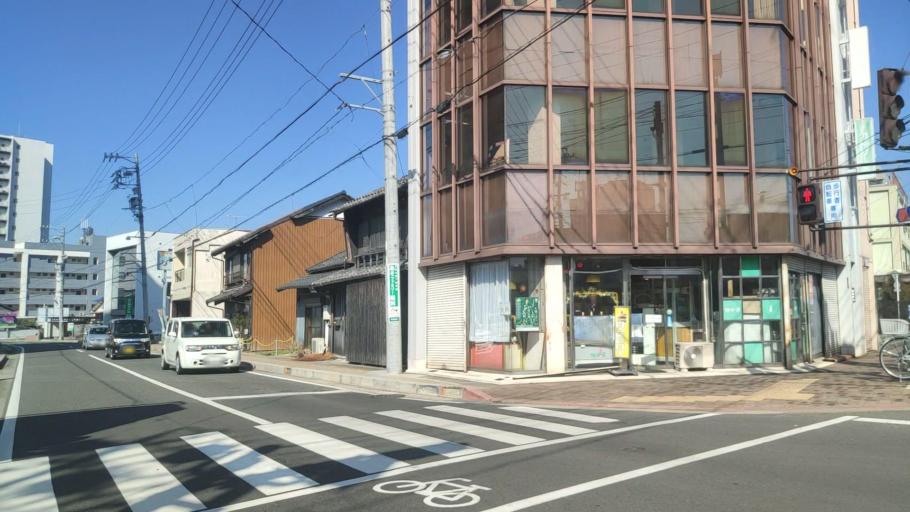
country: JP
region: Gifu
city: Gifu-shi
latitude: 35.4461
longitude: 136.7739
